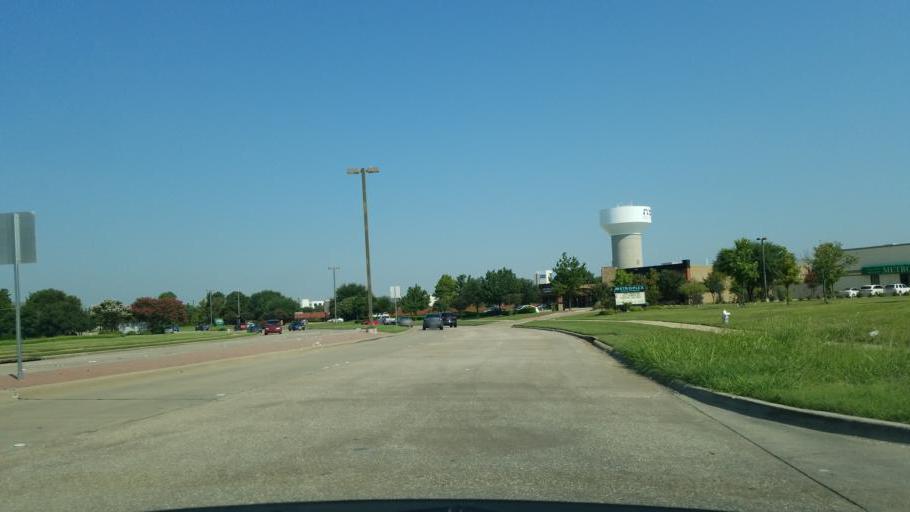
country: US
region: Texas
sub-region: Collin County
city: Allen
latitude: 33.0895
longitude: -96.6724
